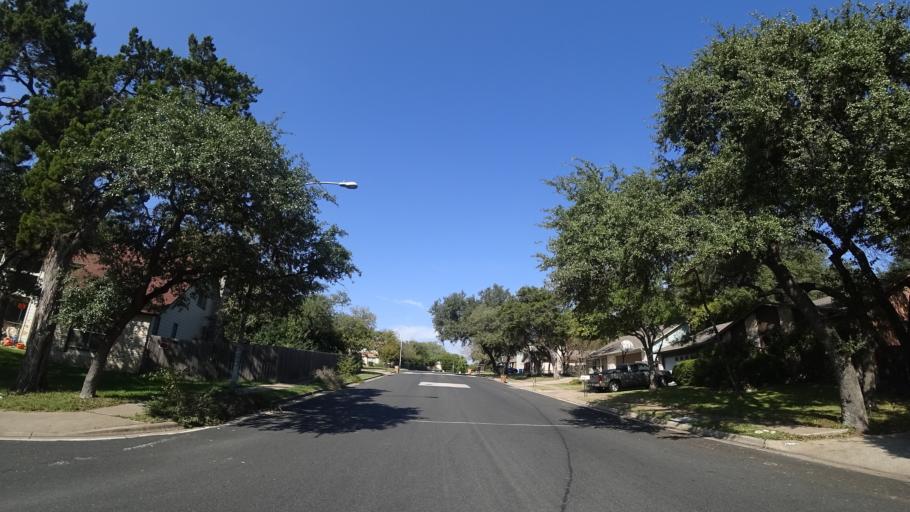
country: US
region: Texas
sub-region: Travis County
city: Shady Hollow
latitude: 30.1966
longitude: -97.8161
